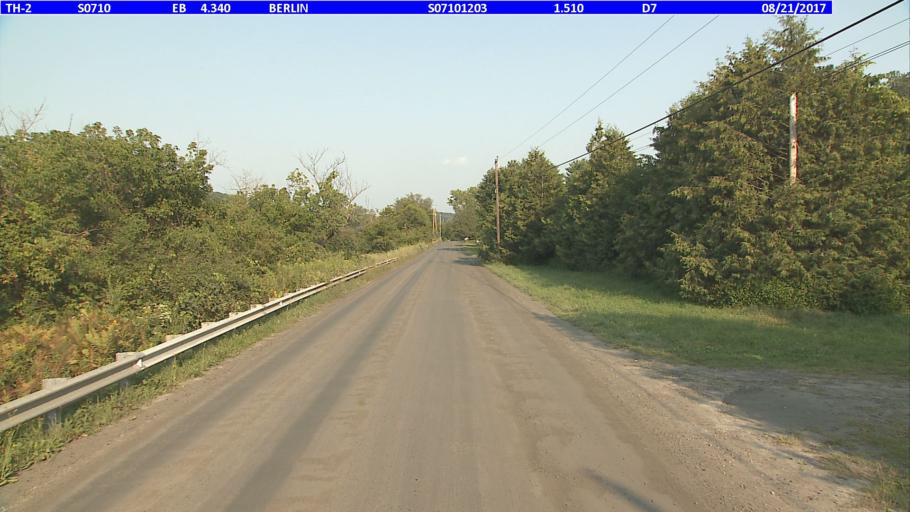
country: US
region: Vermont
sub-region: Washington County
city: Montpelier
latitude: 44.2585
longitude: -72.6151
